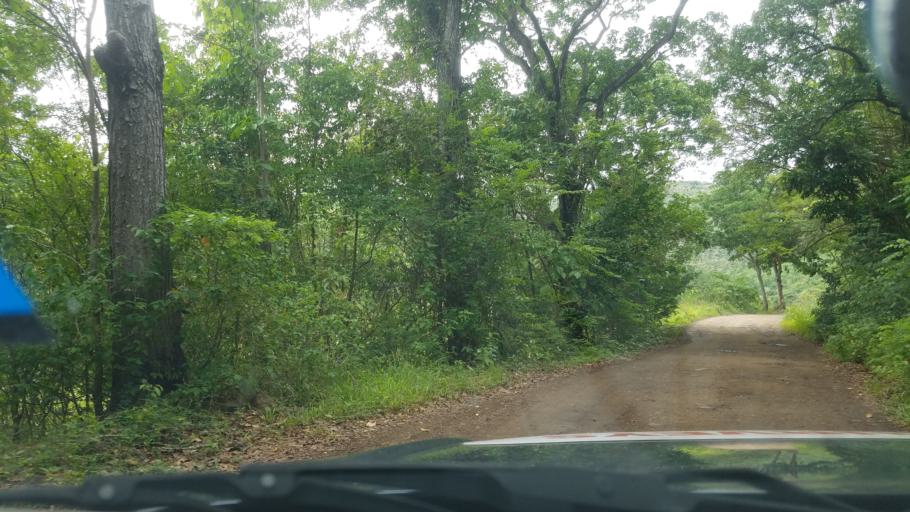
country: LC
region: Gros-Islet
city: Gros Islet
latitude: 14.0222
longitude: -60.9152
